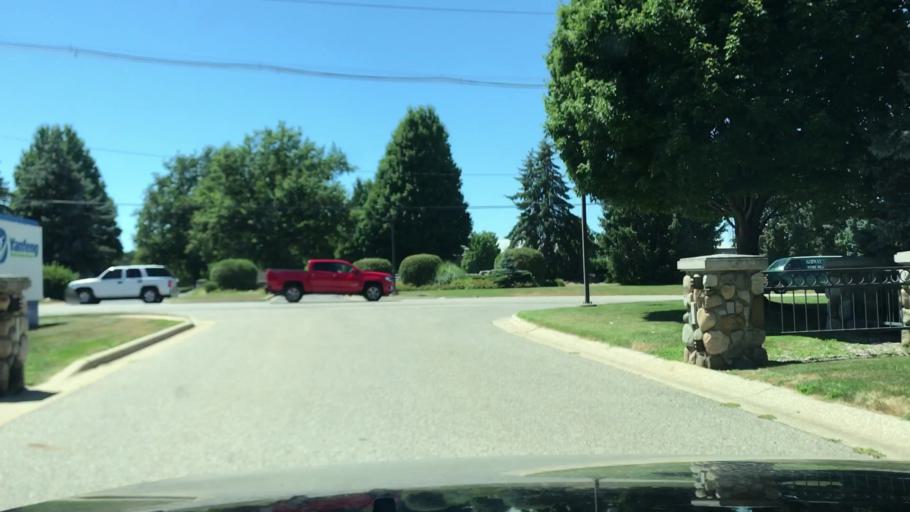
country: US
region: Michigan
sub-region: Ottawa County
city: Holland
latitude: 42.7722
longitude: -86.0769
